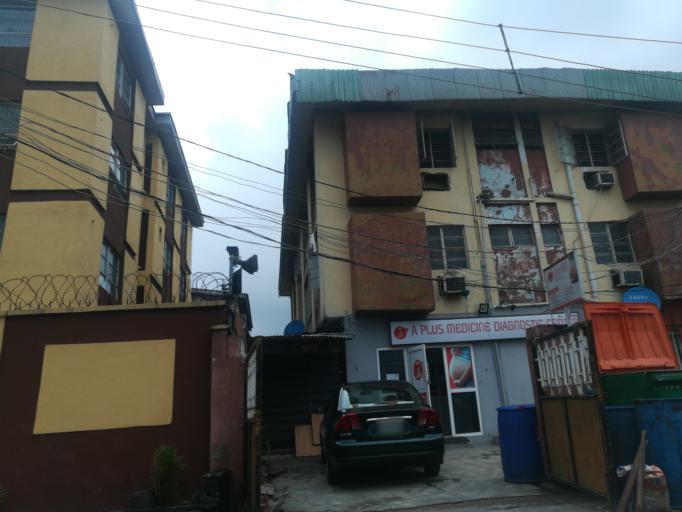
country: NG
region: Lagos
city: Ojota
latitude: 6.5702
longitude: 3.3725
